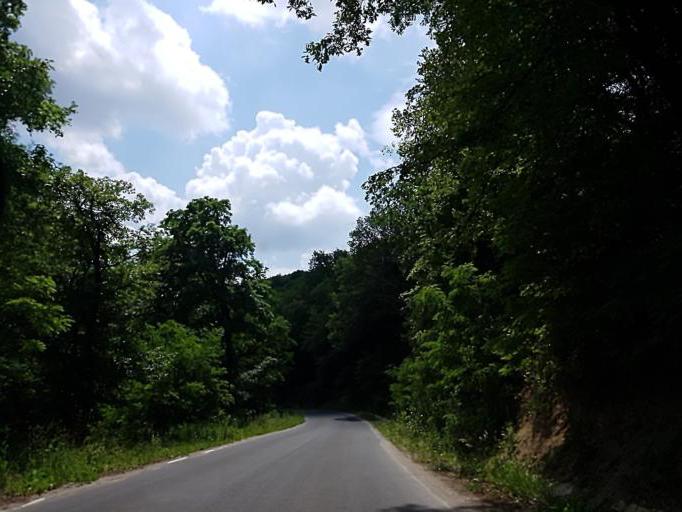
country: RO
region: Sibiu
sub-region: Comuna Seica Mare
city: Seica Mare
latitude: 46.0401
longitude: 24.1587
